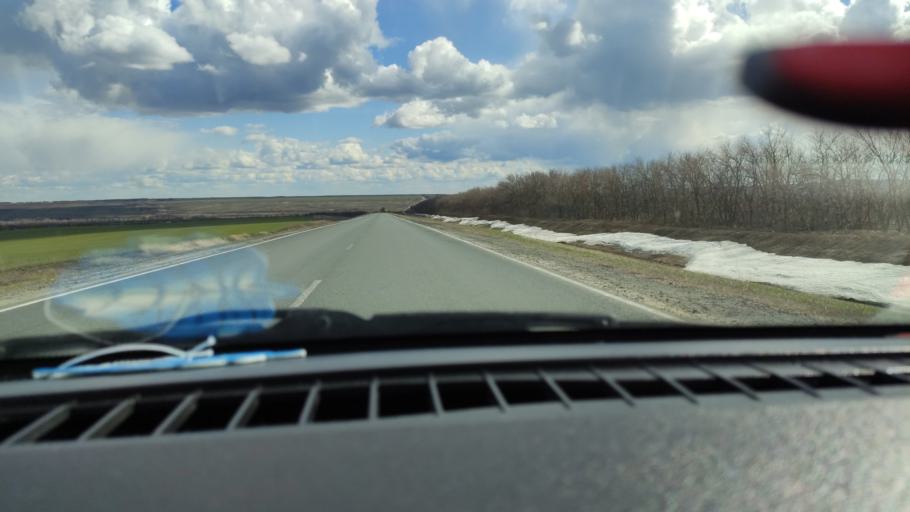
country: RU
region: Saratov
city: Dukhovnitskoye
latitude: 52.7598
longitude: 48.2418
